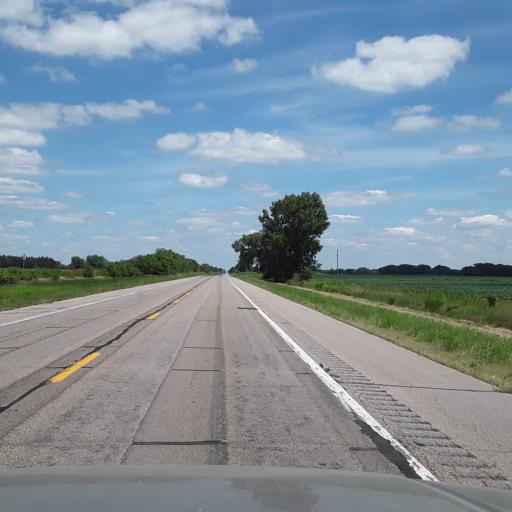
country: US
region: Nebraska
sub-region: Polk County
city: Osceola
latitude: 41.3544
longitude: -97.5733
